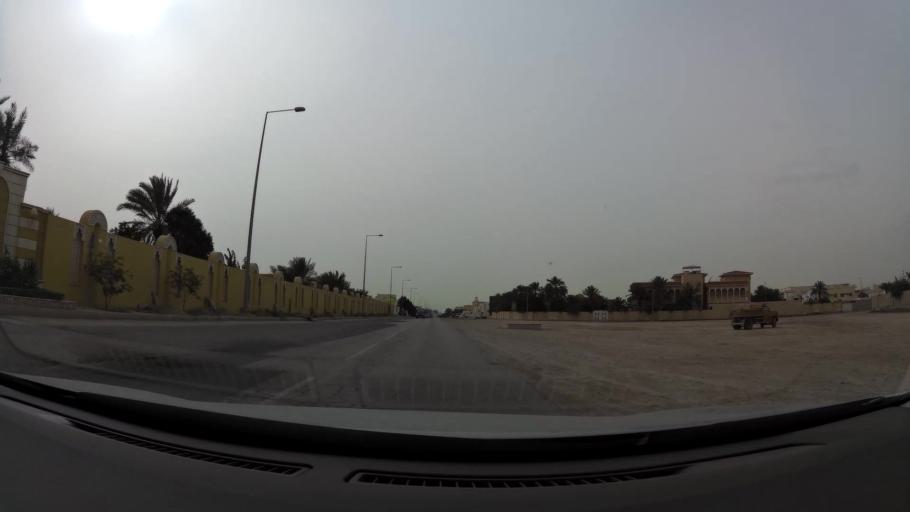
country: QA
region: Baladiyat ad Dawhah
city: Doha
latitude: 25.2487
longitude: 51.5001
